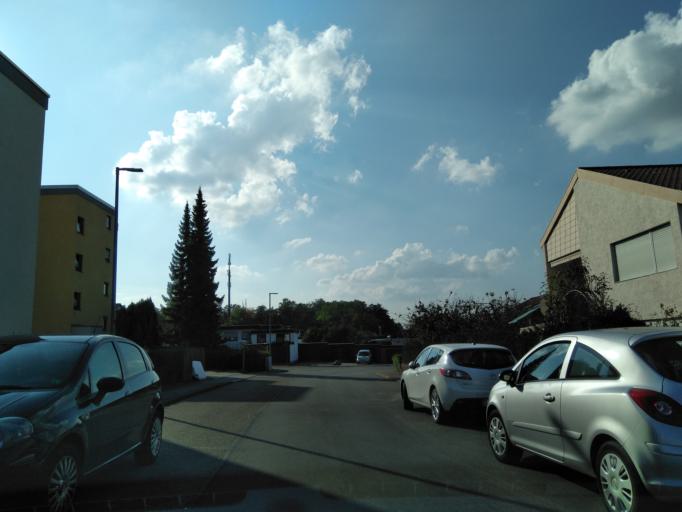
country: DE
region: Baden-Wuerttemberg
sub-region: Regierungsbezirk Stuttgart
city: Sersheim
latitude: 48.9541
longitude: 9.0160
